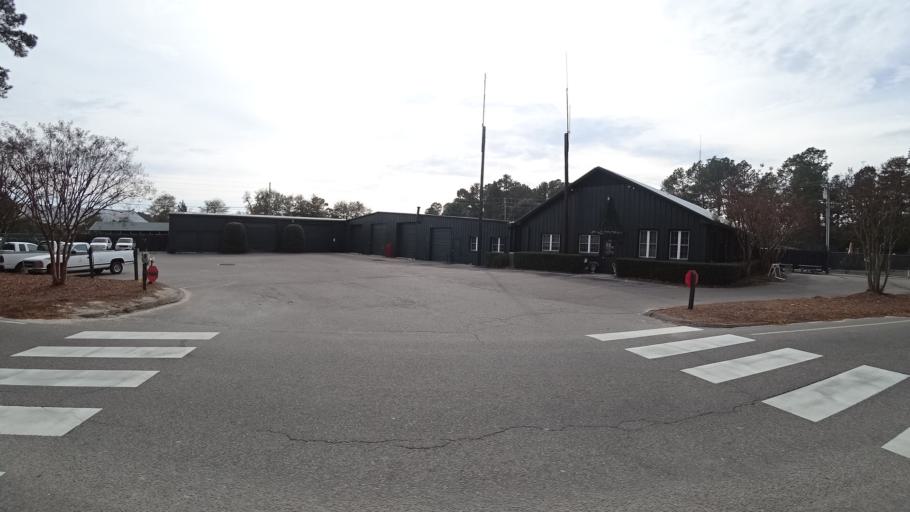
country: US
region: North Carolina
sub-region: Moore County
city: Pinehurst
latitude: 35.1847
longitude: -79.4666
